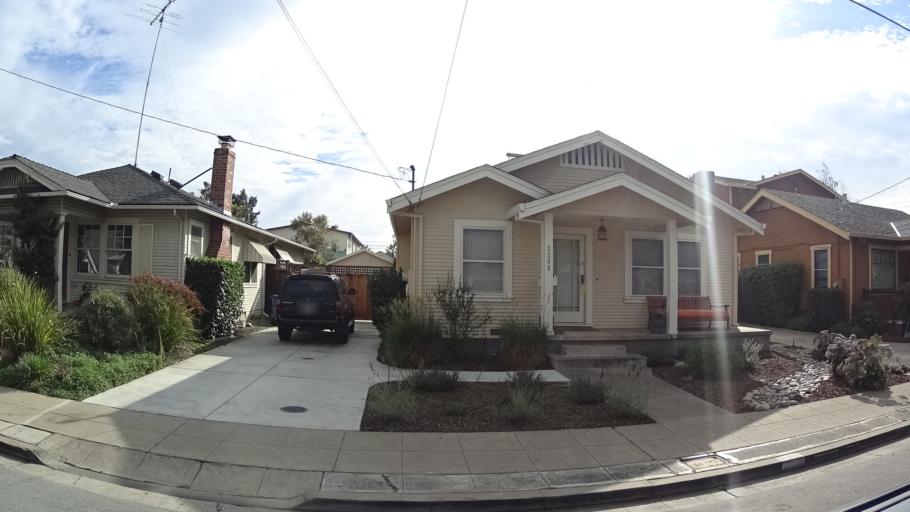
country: US
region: California
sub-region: Santa Clara County
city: Burbank
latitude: 37.3250
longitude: -121.9338
